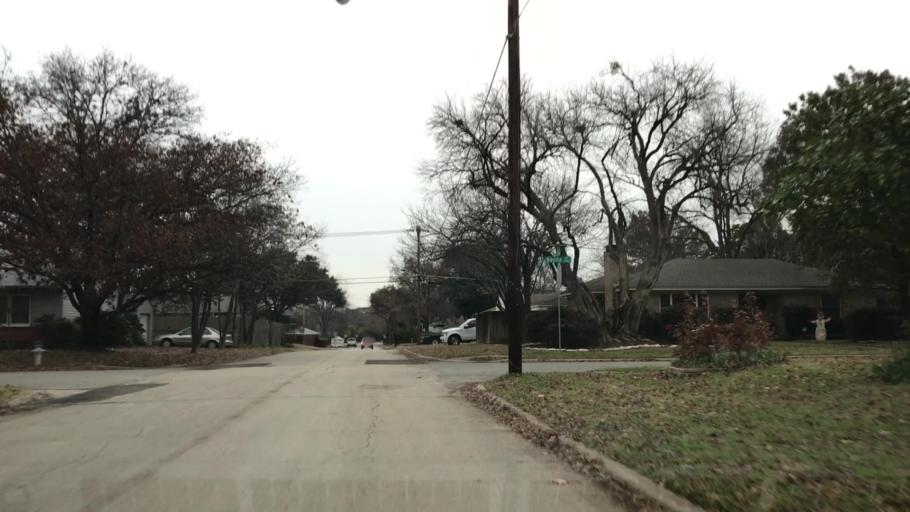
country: US
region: Texas
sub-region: Dallas County
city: University Park
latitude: 32.8678
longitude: -96.8489
